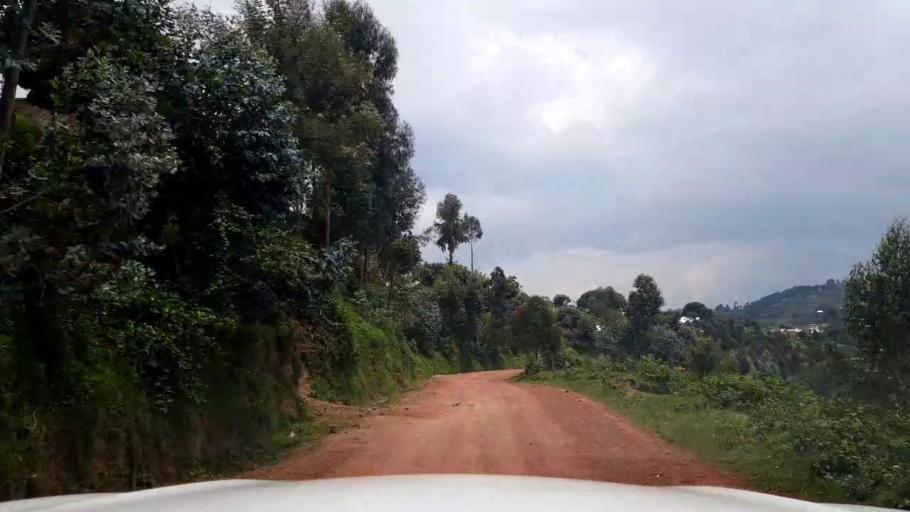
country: RW
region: Northern Province
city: Byumba
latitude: -1.4938
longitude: 29.9336
